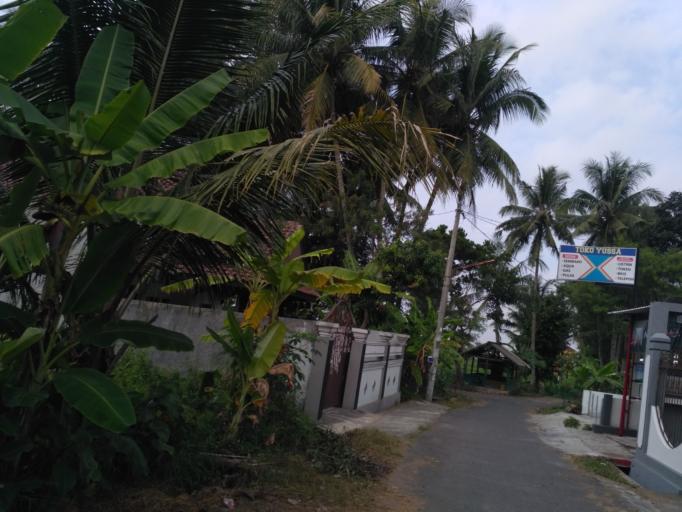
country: ID
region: Daerah Istimewa Yogyakarta
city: Melati
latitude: -7.7066
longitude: 110.4078
